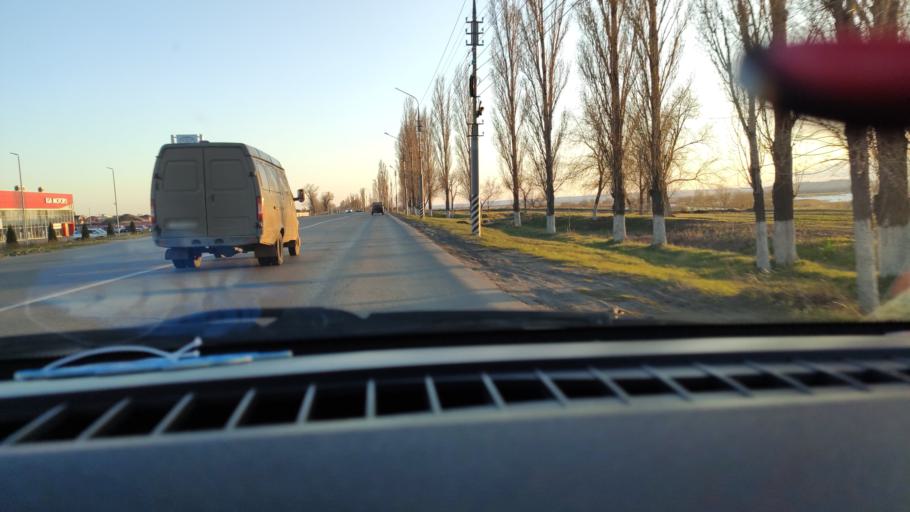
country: RU
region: Saratov
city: Privolzhskiy
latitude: 51.4412
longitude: 46.0680
